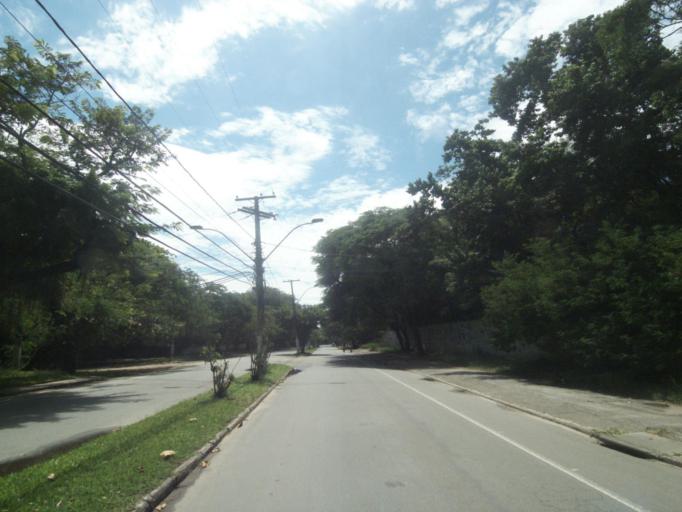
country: BR
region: Rio de Janeiro
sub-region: Niteroi
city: Niteroi
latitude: -22.9689
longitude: -43.0423
